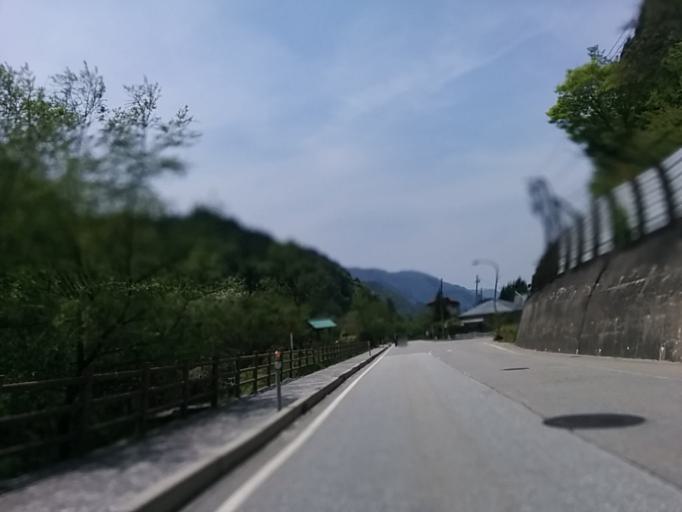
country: JP
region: Gifu
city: Takayama
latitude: 36.2455
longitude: 137.5270
